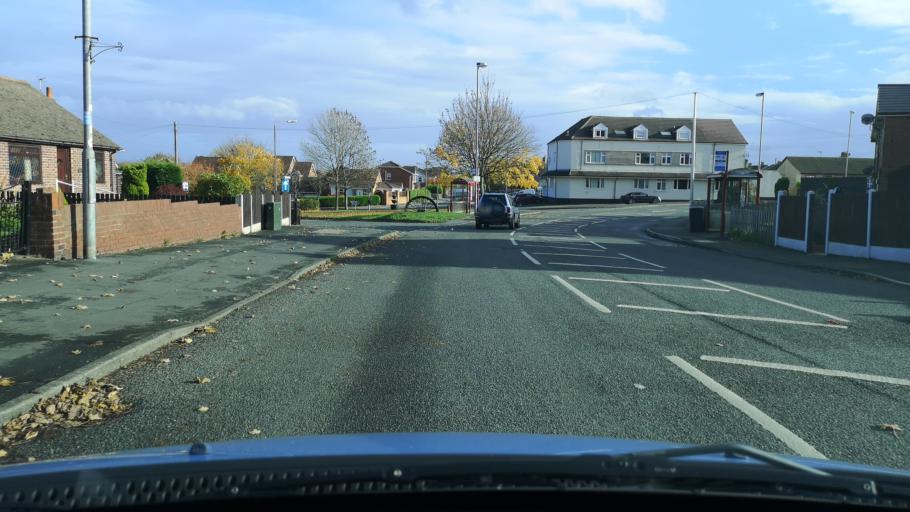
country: GB
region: England
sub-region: City and Borough of Wakefield
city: Crofton
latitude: 53.6519
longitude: -1.4182
